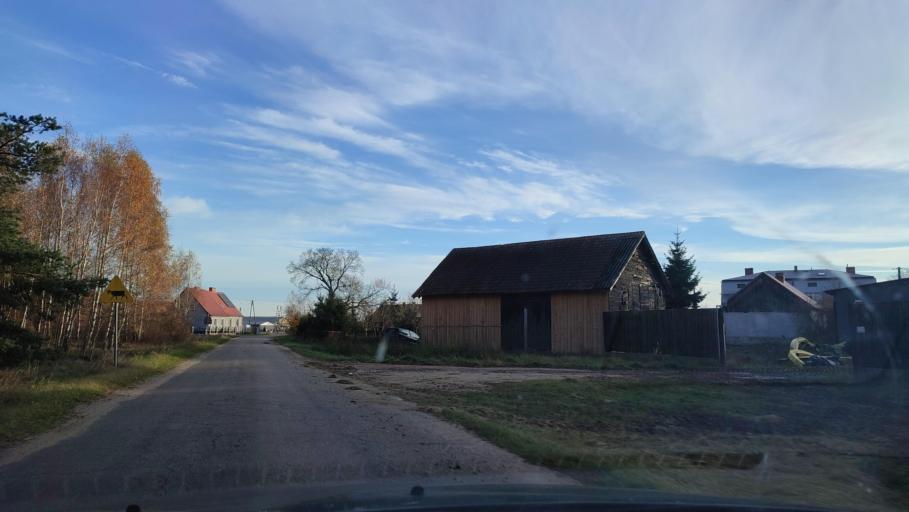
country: PL
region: Masovian Voivodeship
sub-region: Powiat przasnyski
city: Chorzele
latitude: 53.3417
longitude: 20.7534
